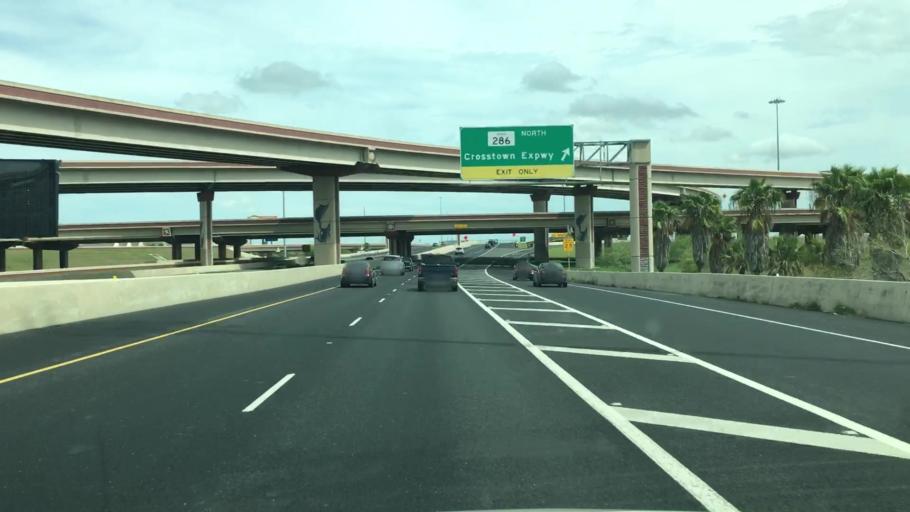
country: US
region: Texas
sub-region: Nueces County
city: Corpus Christi
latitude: 27.7379
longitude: -97.4320
